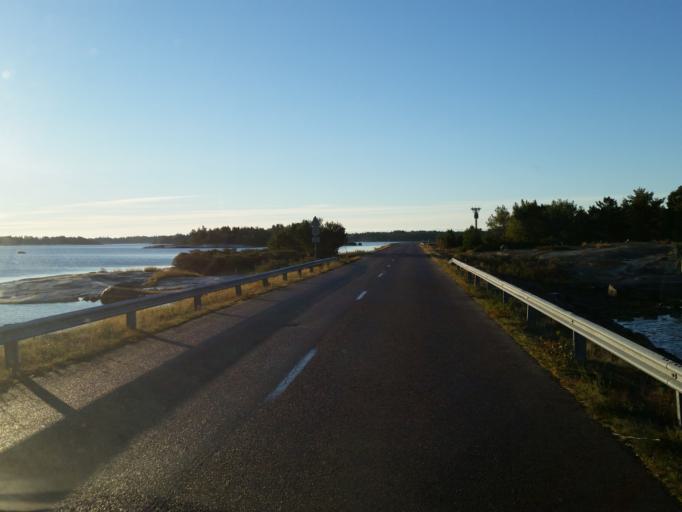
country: AX
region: Alands skaergard
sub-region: Vardoe
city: Vardoe
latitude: 60.3213
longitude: 20.3732
